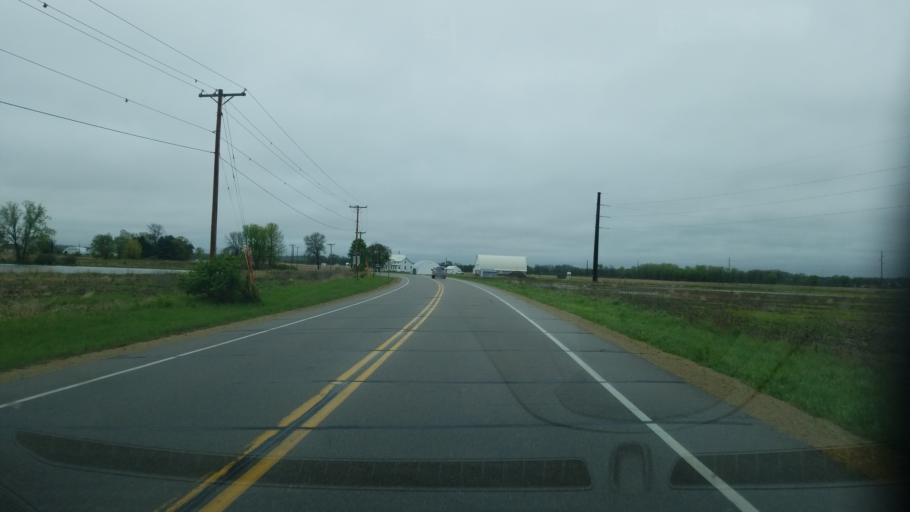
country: US
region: Wisconsin
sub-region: Dane County
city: Fitchburg
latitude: 42.9448
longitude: -89.4385
